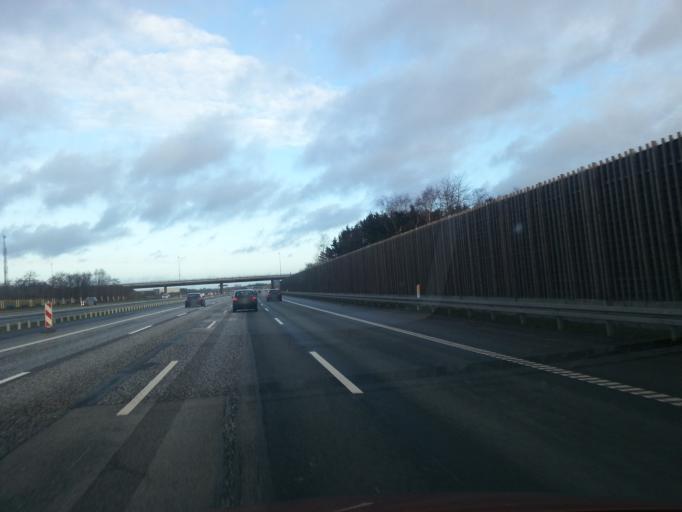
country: DK
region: Zealand
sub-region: Solrod Kommune
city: Solrod Strand
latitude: 55.5716
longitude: 12.2433
